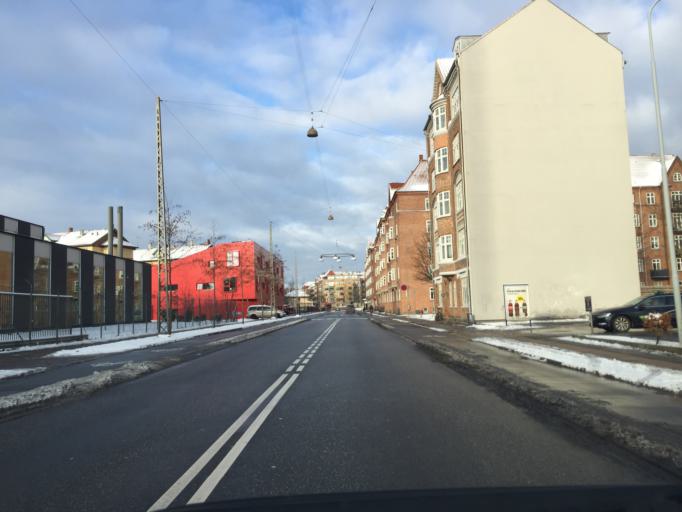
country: DK
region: Capital Region
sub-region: Kobenhavn
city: Christianshavn
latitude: 55.6599
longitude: 12.5997
